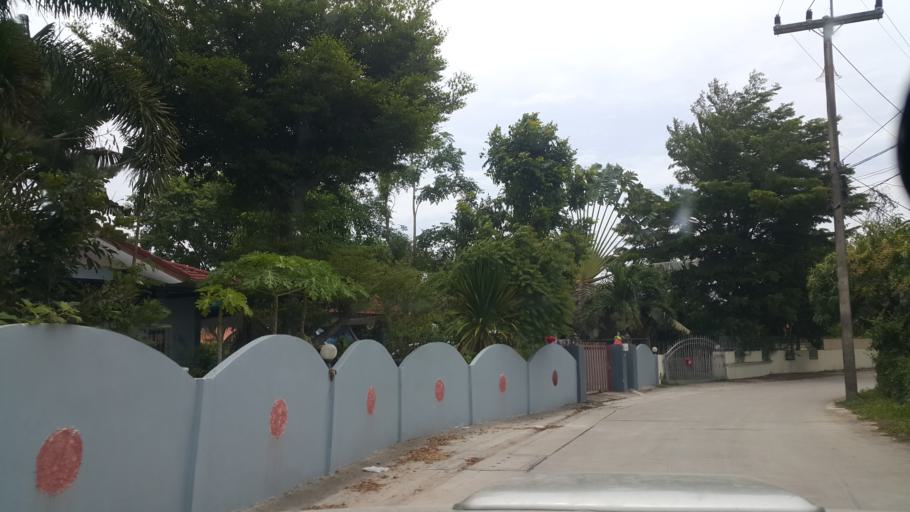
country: TH
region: Rayong
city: Ban Chang
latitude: 12.7166
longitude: 101.0646
